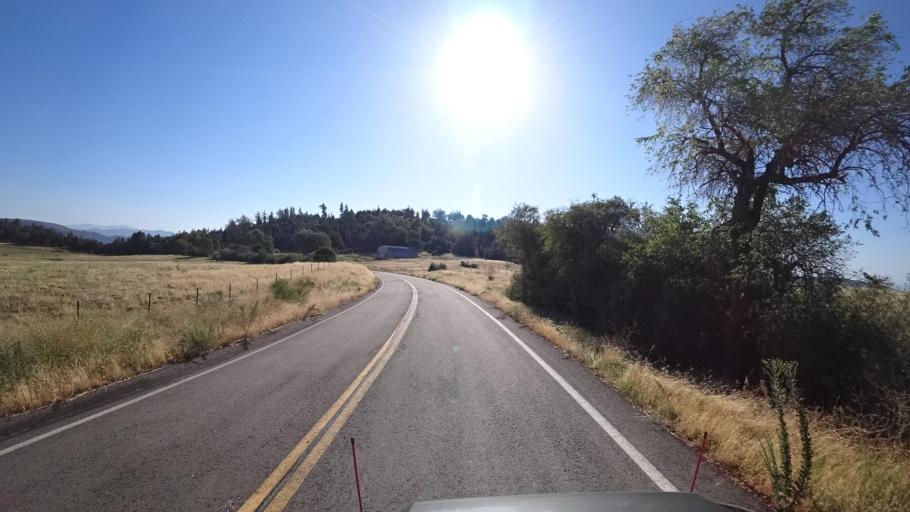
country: US
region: California
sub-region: Riverside County
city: Aguanga
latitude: 33.2868
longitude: -116.8153
